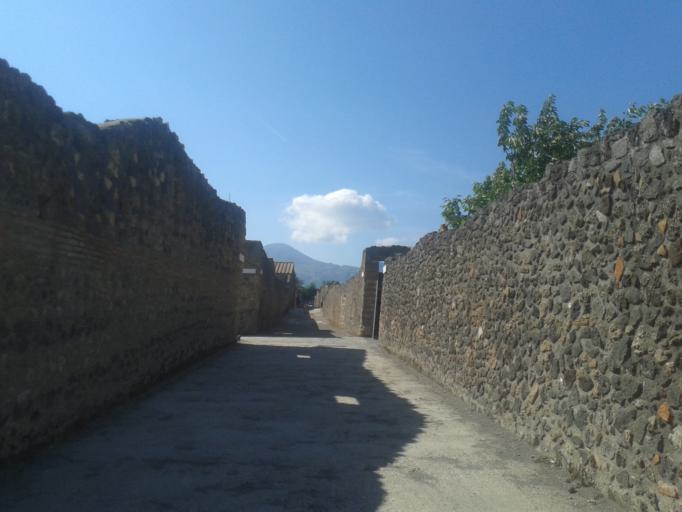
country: IT
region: Campania
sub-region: Provincia di Napoli
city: Pompei
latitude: 40.7499
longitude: 14.4926
